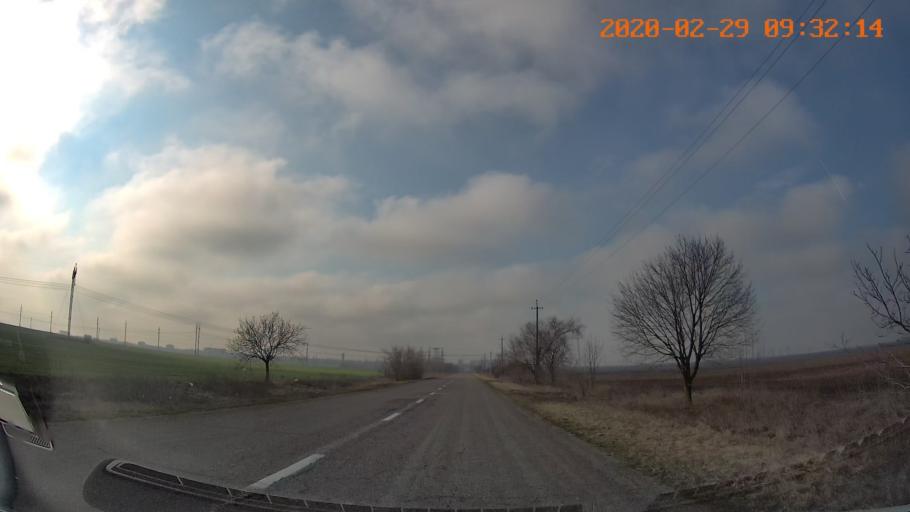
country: MD
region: Telenesti
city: Dnestrovsc
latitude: 46.6420
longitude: 29.9070
